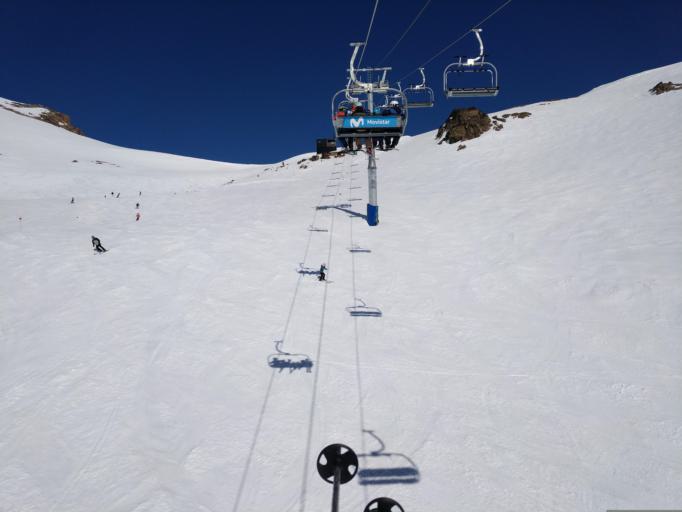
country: AR
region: Rio Negro
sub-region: Departamento de Bariloche
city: San Carlos de Bariloche
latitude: -41.1723
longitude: -71.4825
